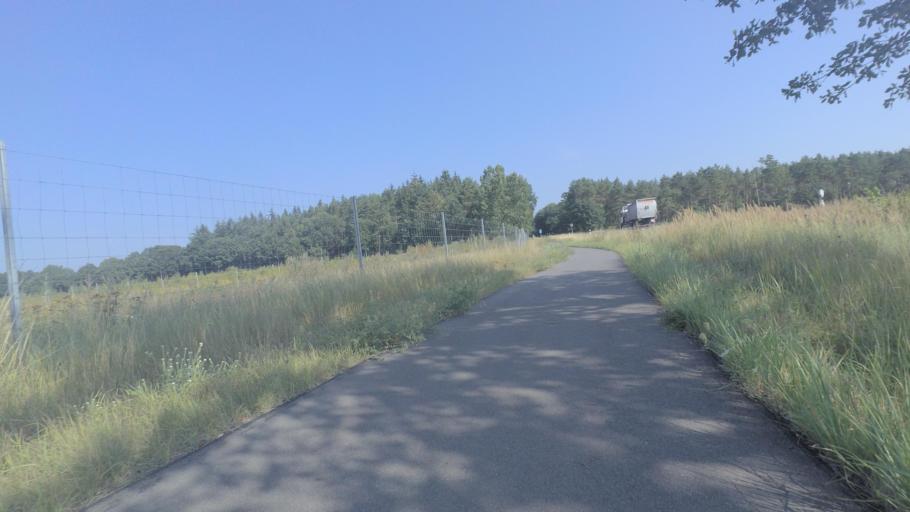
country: DE
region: Mecklenburg-Vorpommern
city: Malchow
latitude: 53.4993
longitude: 12.4219
